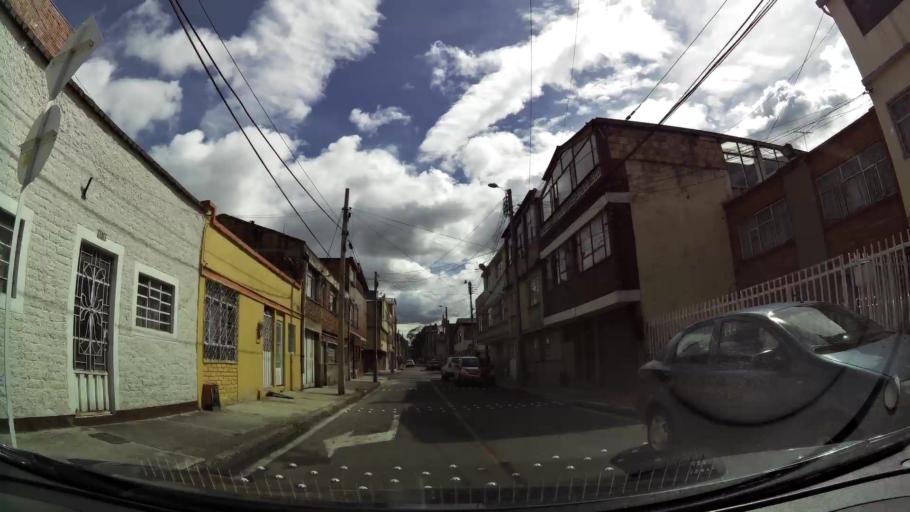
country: CO
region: Bogota D.C.
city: Barrio San Luis
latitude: 4.6783
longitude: -74.0646
